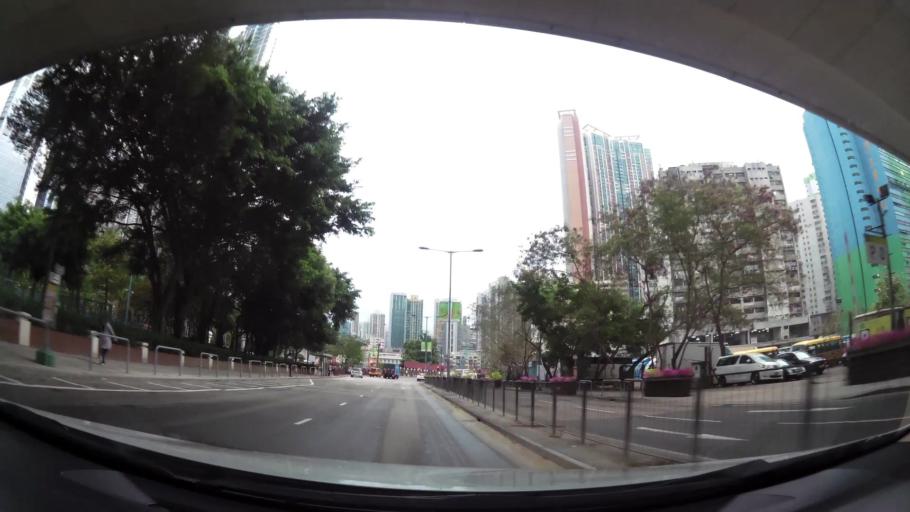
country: HK
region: Tsuen Wan
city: Tsuen Wan
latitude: 22.3659
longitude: 114.1137
